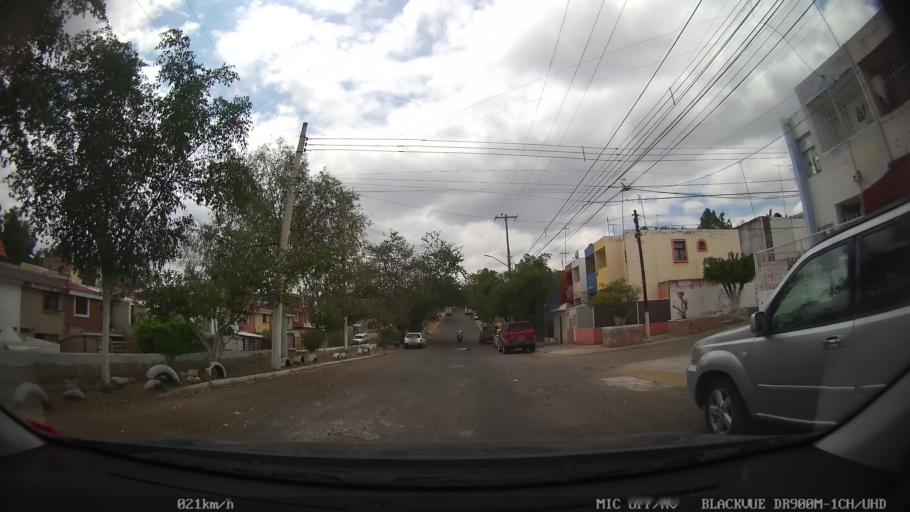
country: MX
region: Jalisco
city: Tonala
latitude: 20.6314
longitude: -103.2586
